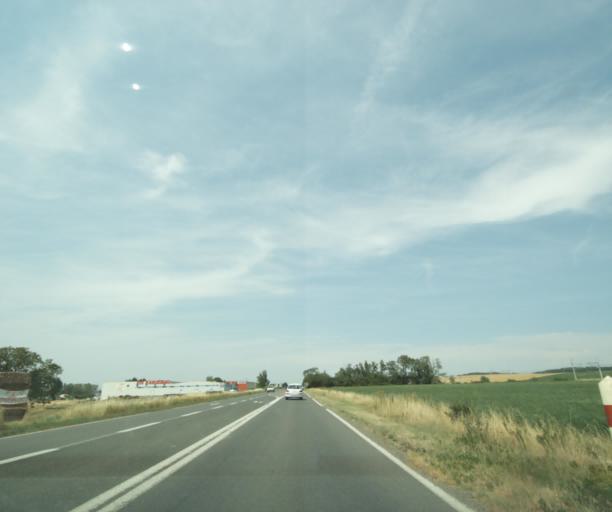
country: FR
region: Poitou-Charentes
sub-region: Departement de la Vienne
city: Les Ormes
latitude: 46.9579
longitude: 0.6076
